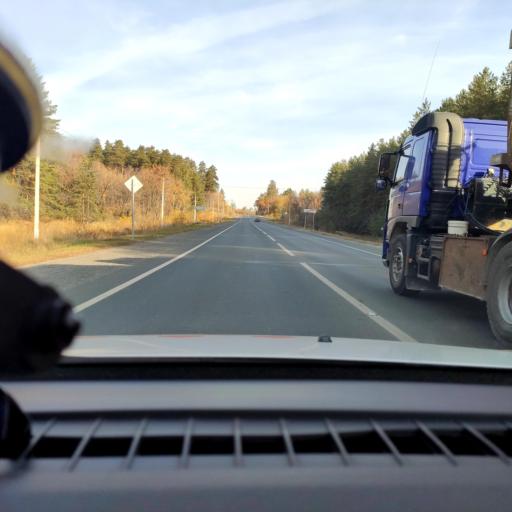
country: RU
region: Samara
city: Volzhskiy
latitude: 53.4414
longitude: 50.1237
